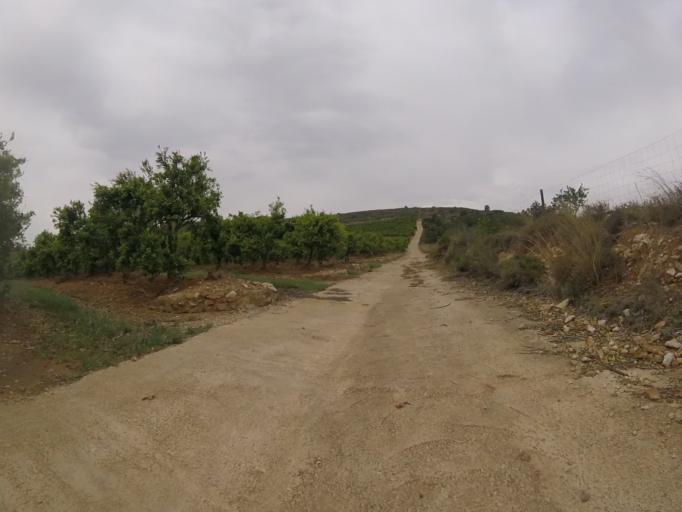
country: ES
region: Valencia
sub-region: Provincia de Castello
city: Alcala de Xivert
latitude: 40.2792
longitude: 0.2530
